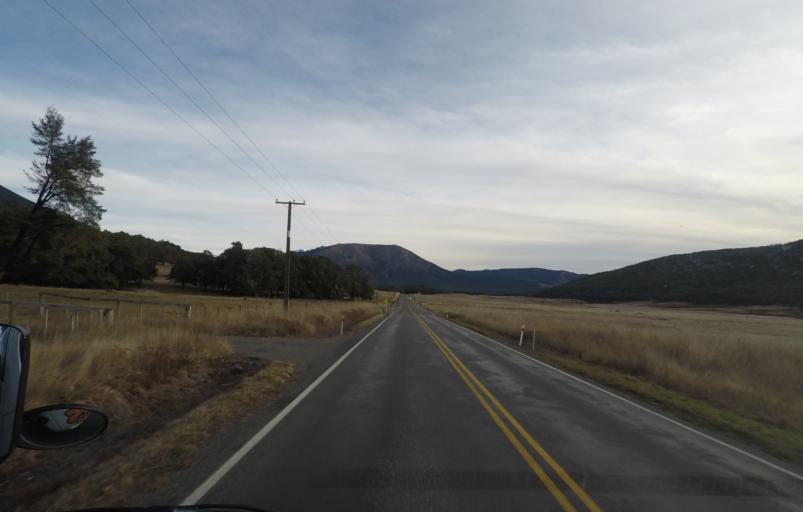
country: NZ
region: Tasman
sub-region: Tasman District
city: Wakefield
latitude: -41.7941
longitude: 172.8772
